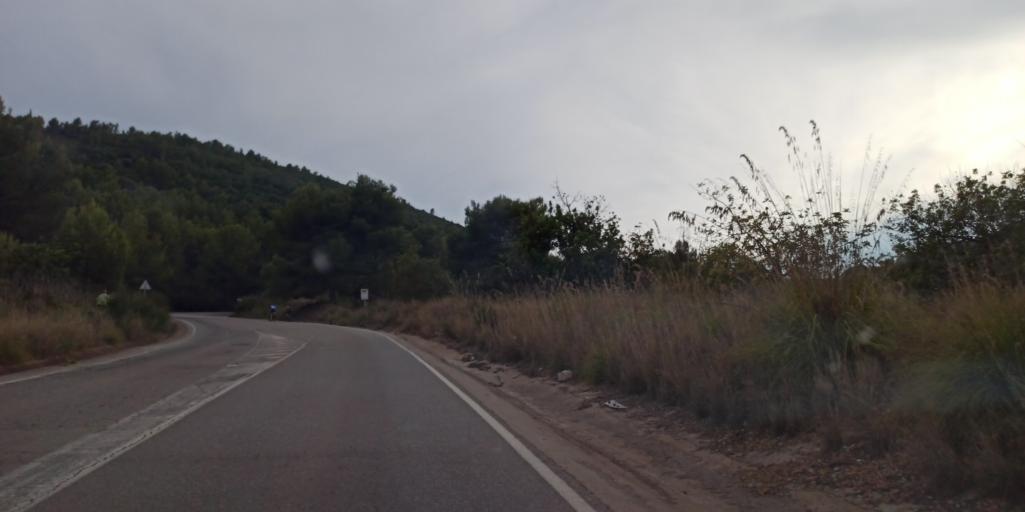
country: ES
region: Catalonia
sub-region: Provincia de Barcelona
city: Castelldefels
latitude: 41.2964
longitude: 1.9711
